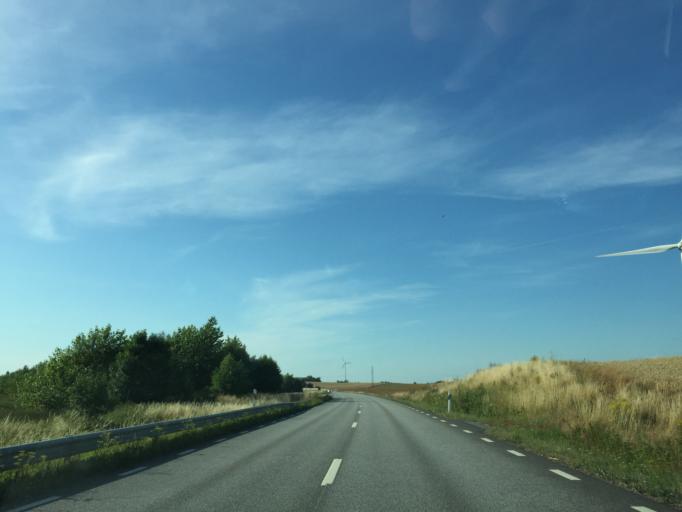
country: SE
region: Skane
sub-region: Svedala Kommun
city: Klagerup
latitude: 55.6101
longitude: 13.2656
